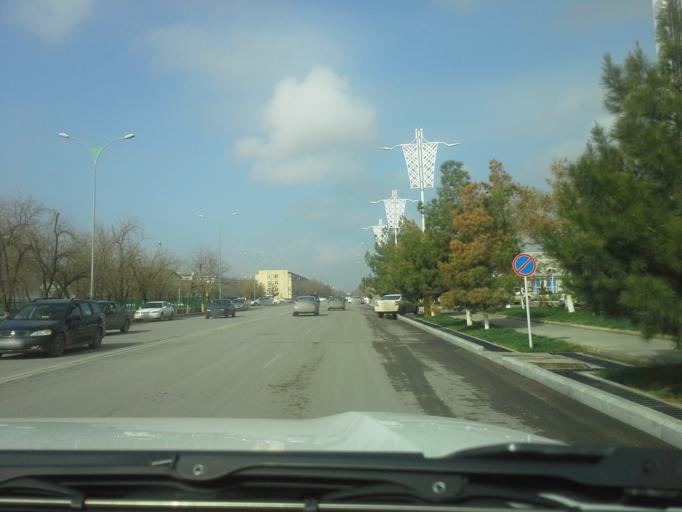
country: TM
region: Mary
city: Mary
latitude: 37.5916
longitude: 61.8366
